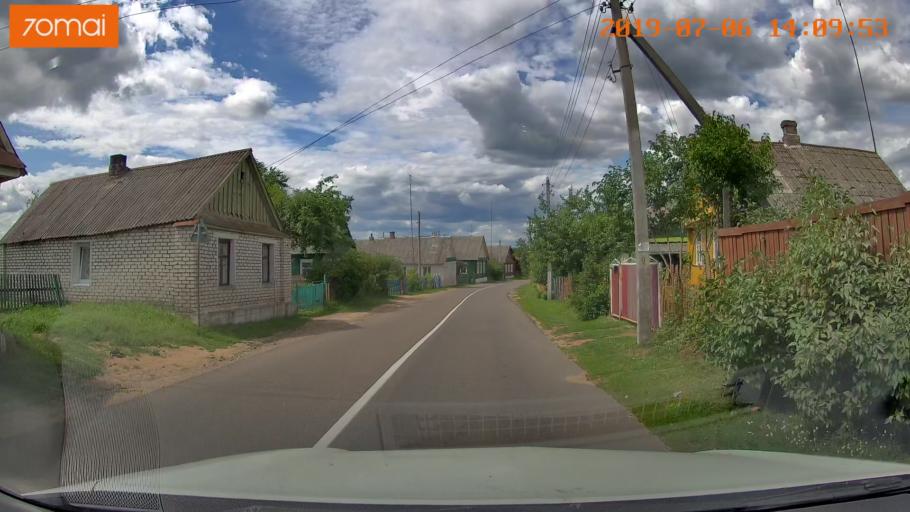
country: BY
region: Minsk
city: Ivyanyets
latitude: 53.8832
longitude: 26.7472
